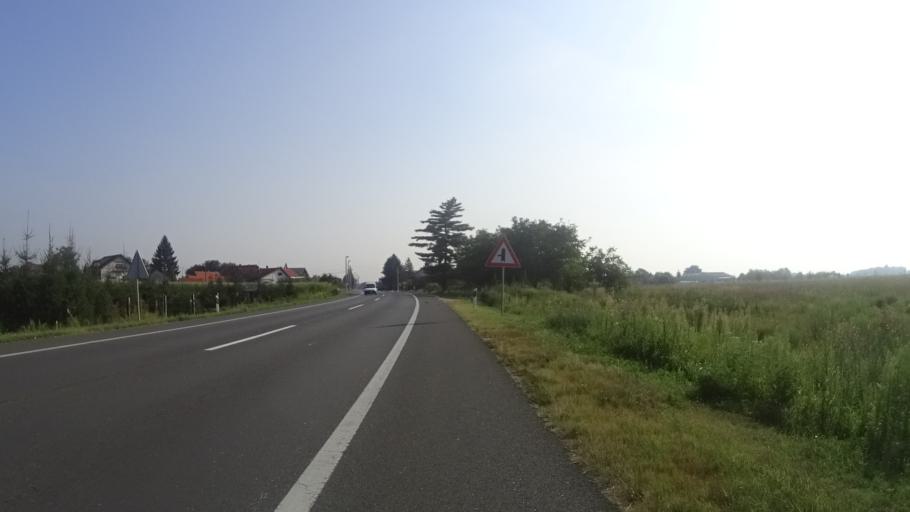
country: HR
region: Medimurska
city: Nedelisce
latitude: 46.3671
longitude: 16.3719
